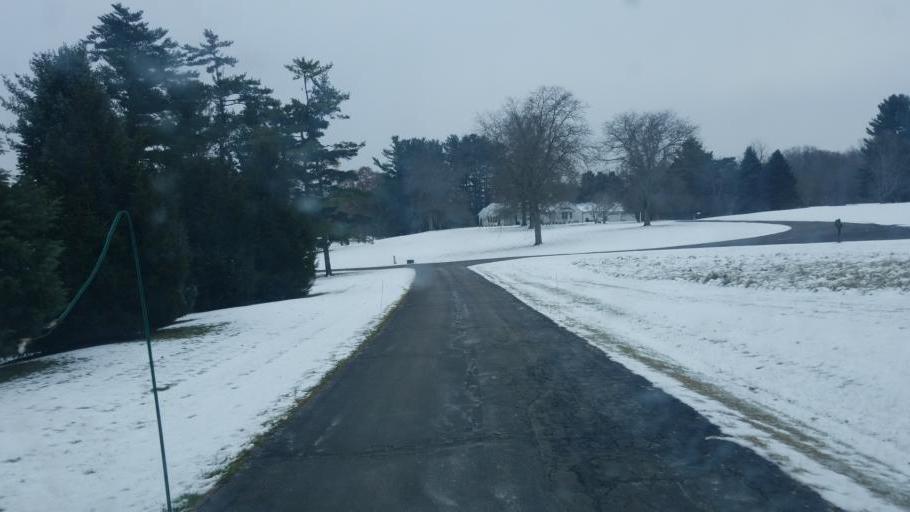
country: US
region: Ohio
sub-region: Richland County
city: Ontario
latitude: 40.7411
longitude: -82.5754
